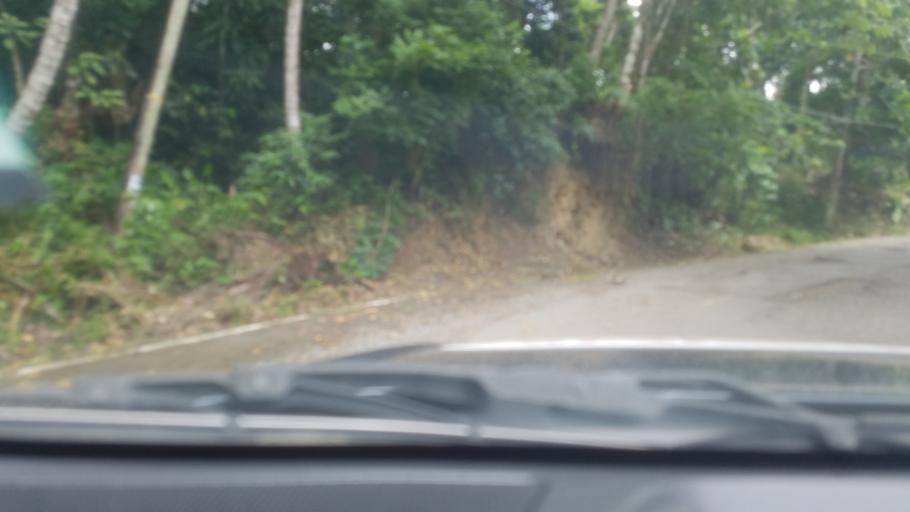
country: LC
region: Micoud Quarter
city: Micoud
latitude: 13.7967
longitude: -60.9506
